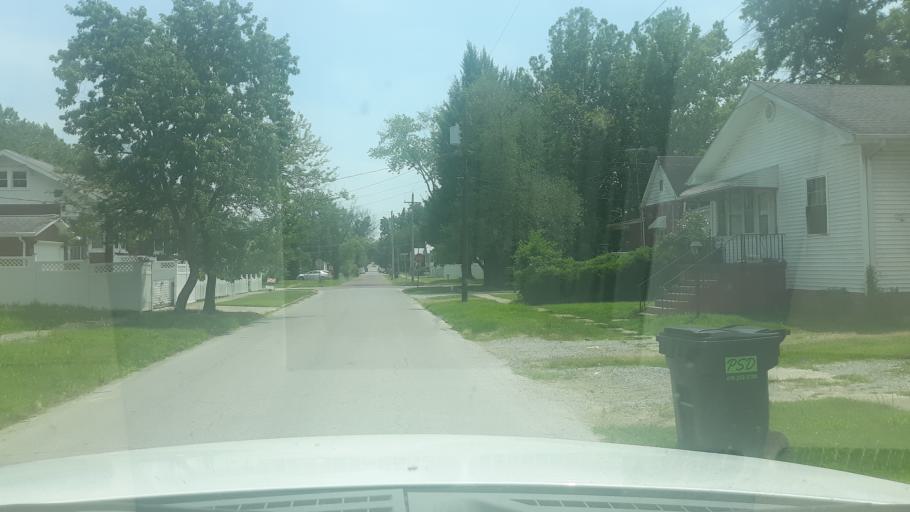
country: US
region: Illinois
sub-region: Saline County
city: Harrisburg
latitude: 37.7351
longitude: -88.5436
